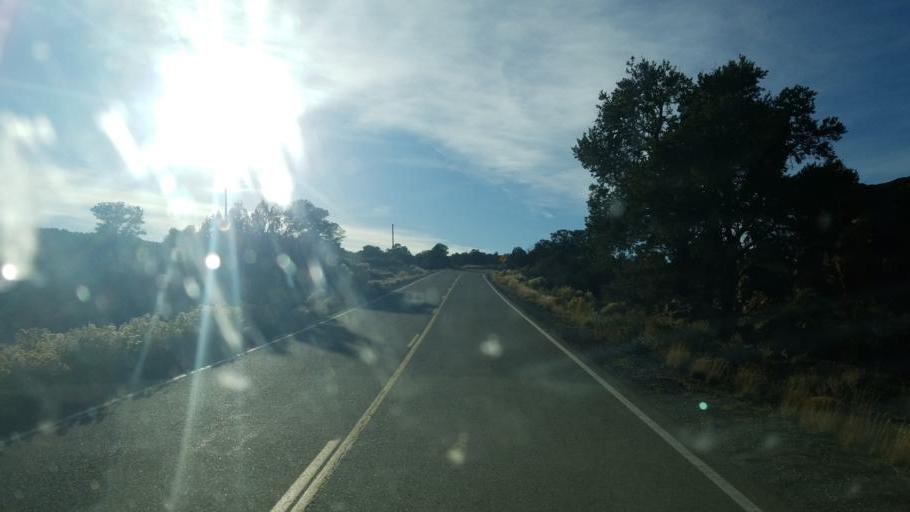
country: US
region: New Mexico
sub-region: San Juan County
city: Bloomfield
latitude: 36.7277
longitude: -107.6683
